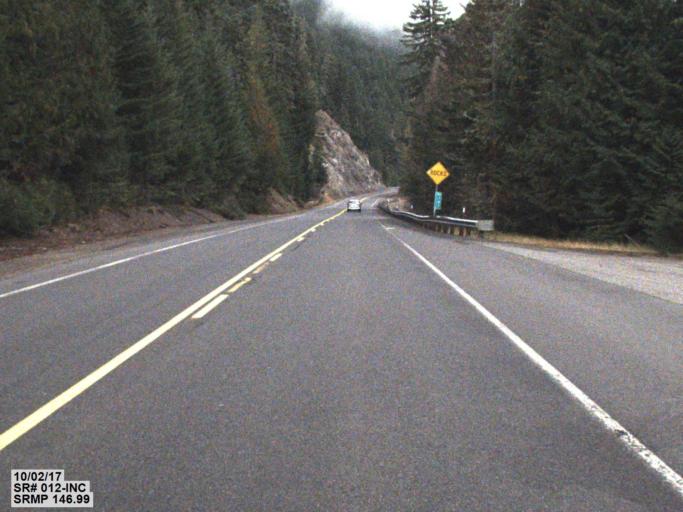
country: US
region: Washington
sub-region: Yakima County
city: Tieton
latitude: 46.6394
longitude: -121.4549
